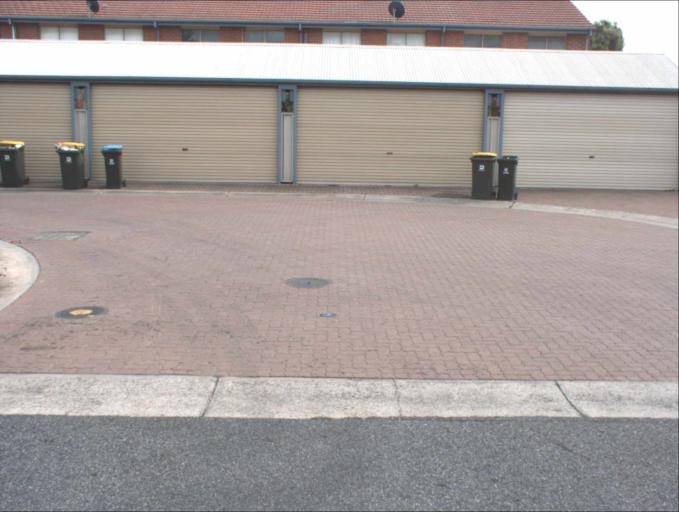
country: AU
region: South Australia
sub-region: Port Adelaide Enfield
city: Birkenhead
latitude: -34.8314
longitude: 138.4984
